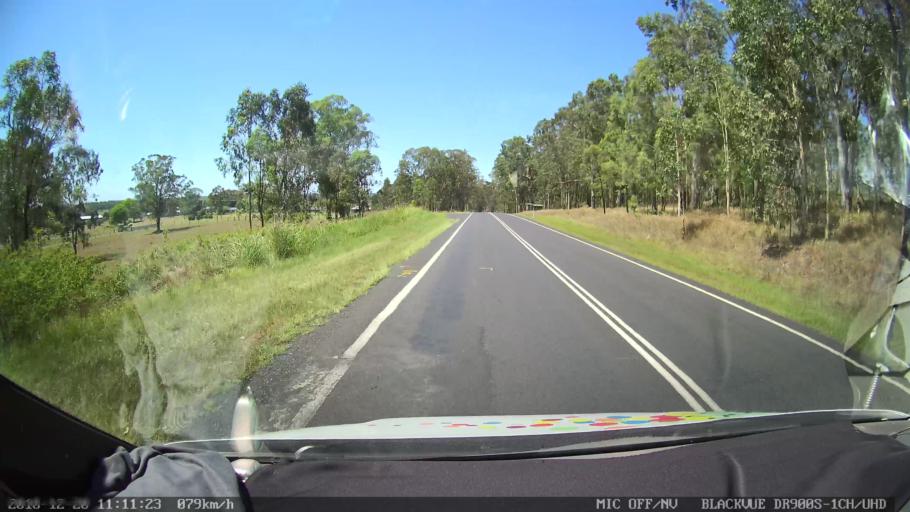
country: AU
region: New South Wales
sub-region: Richmond Valley
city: Casino
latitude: -28.9603
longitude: 153.0136
